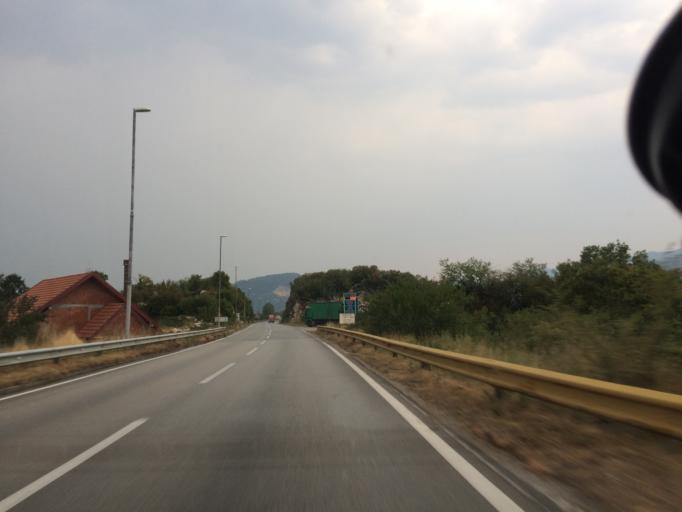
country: ME
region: Opstina Niksic
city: Niksic
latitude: 42.7578
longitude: 18.9397
